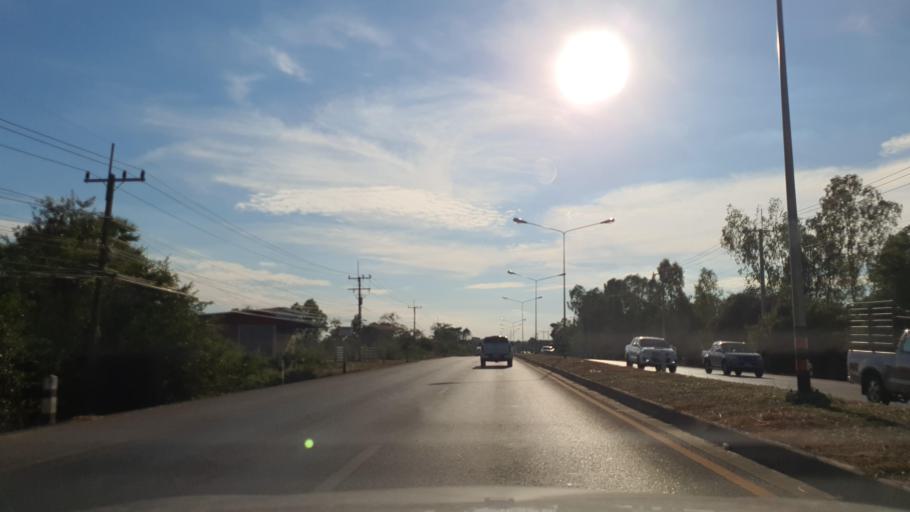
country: TH
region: Maha Sarakham
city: Kantharawichai
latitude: 16.3423
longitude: 103.3167
